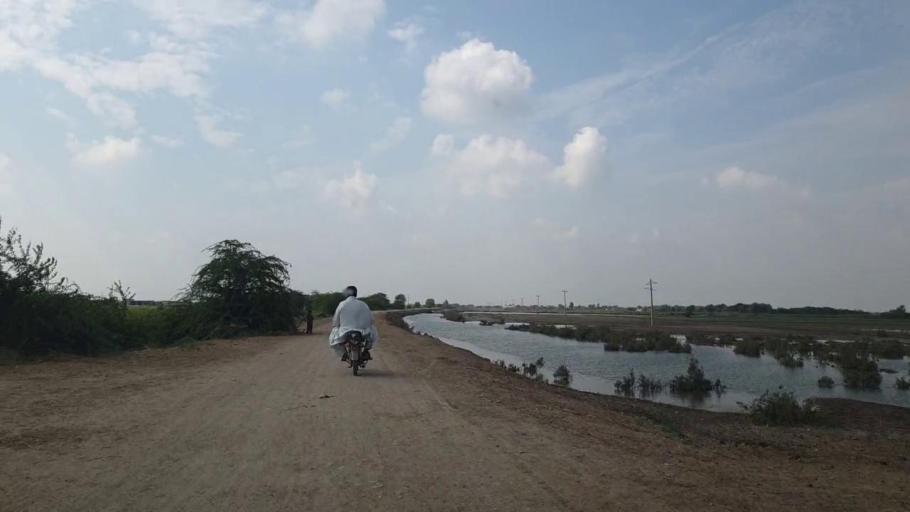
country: PK
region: Sindh
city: Badin
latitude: 24.5068
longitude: 68.6557
